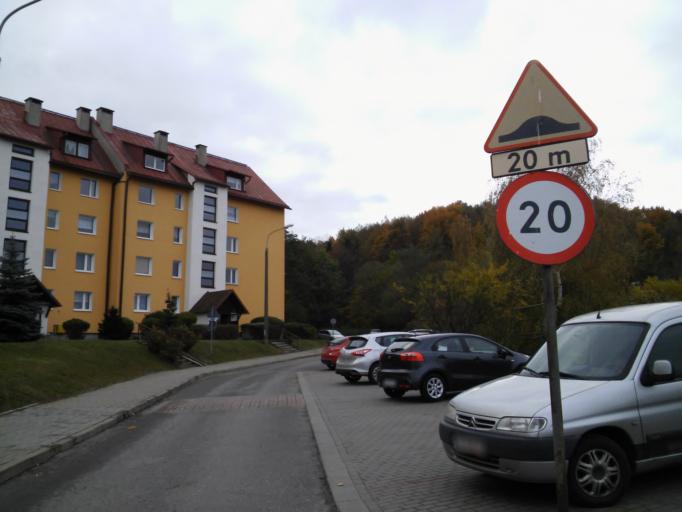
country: PL
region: Pomeranian Voivodeship
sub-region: Gdansk
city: Gdansk
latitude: 54.3775
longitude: 18.5877
